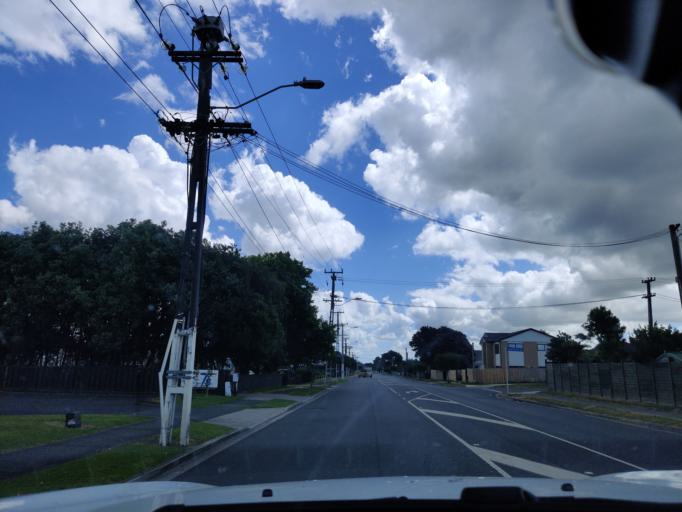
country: NZ
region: Auckland
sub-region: Auckland
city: Red Hill
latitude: -37.0565
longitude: 174.9566
